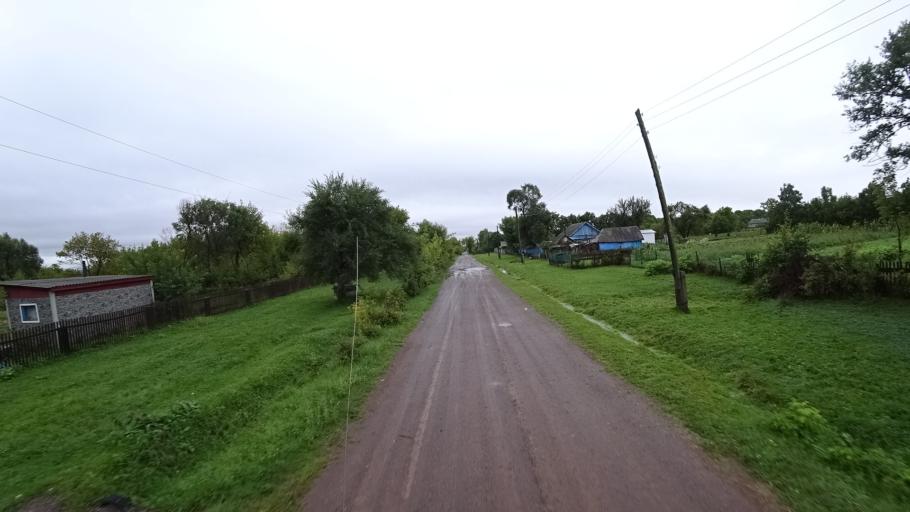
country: RU
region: Primorskiy
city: Monastyrishche
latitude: 44.2620
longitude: 132.4250
